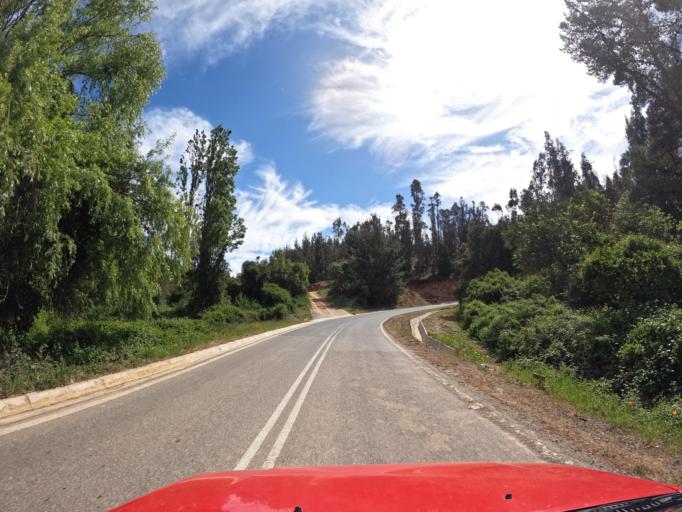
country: CL
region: Maule
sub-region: Provincia de Talca
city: Talca
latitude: -35.0101
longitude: -71.9719
